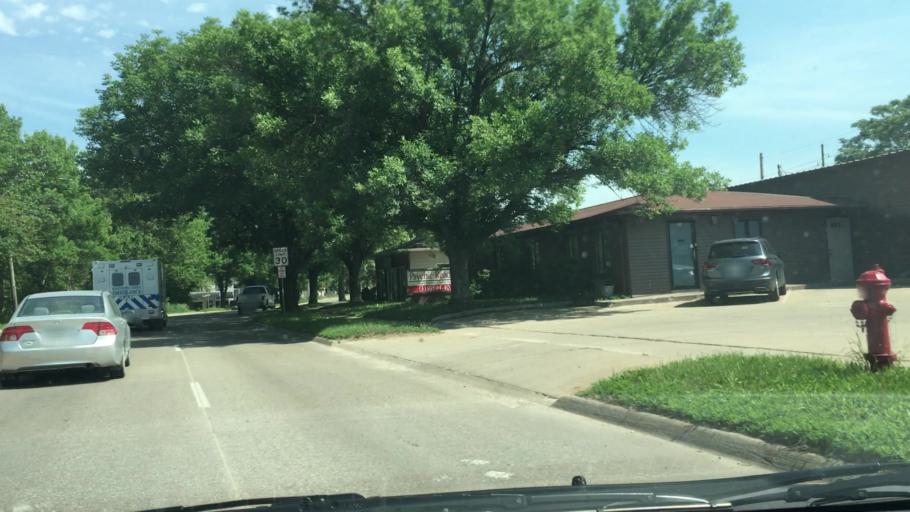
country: US
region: Iowa
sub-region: Johnson County
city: Iowa City
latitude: 41.6498
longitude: -91.5320
